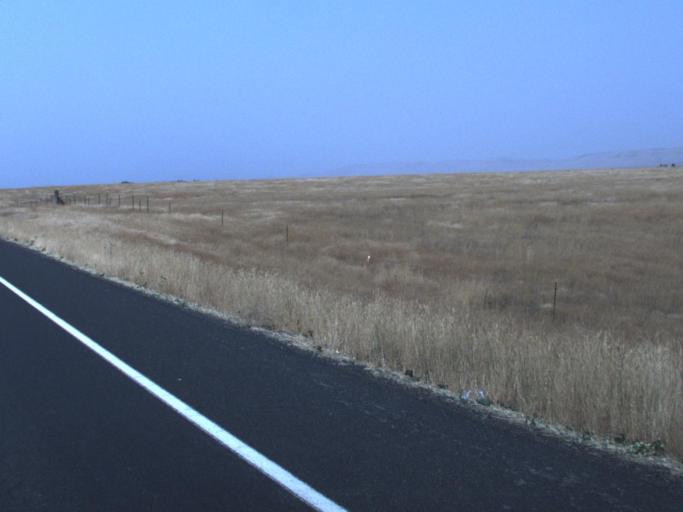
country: US
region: Washington
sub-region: Yakima County
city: Zillah
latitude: 46.5221
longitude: -120.2387
